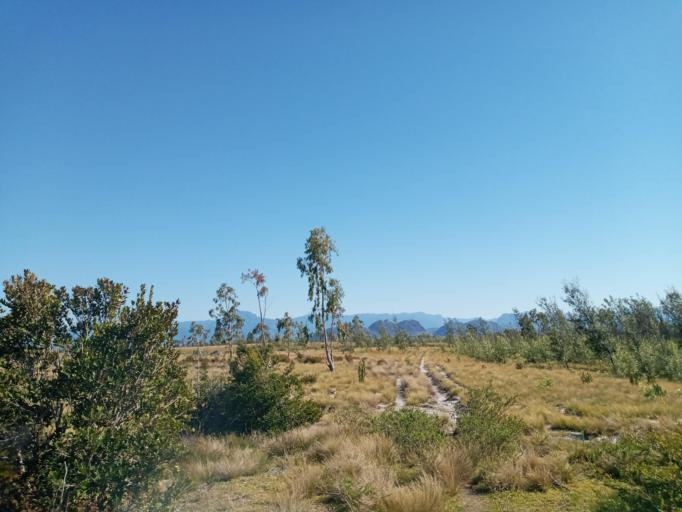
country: MG
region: Atsimo-Atsinanana
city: Vohipaho
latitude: -24.2480
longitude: 47.3177
